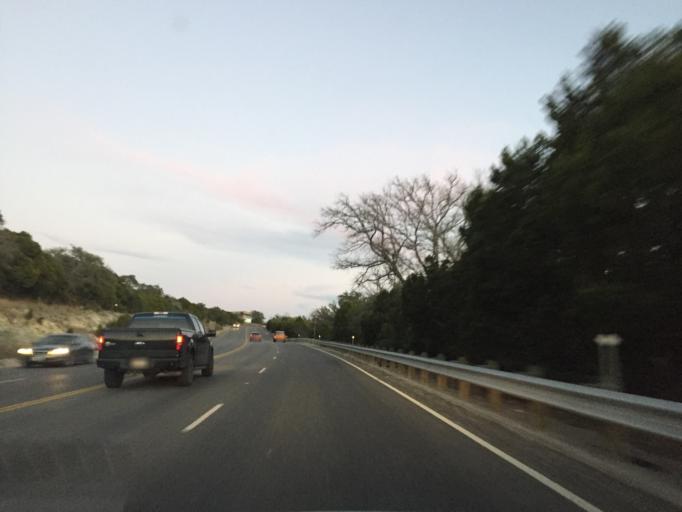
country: US
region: Texas
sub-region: Travis County
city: Jonestown
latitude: 30.5185
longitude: -97.8942
